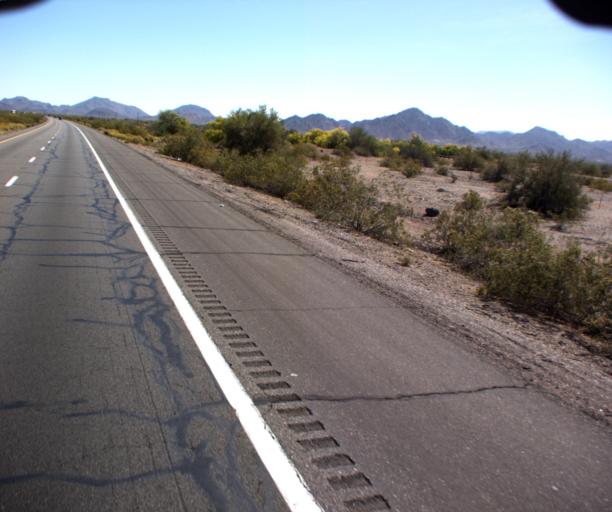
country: US
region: Arizona
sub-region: La Paz County
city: Quartzsite
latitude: 33.6696
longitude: -114.1627
